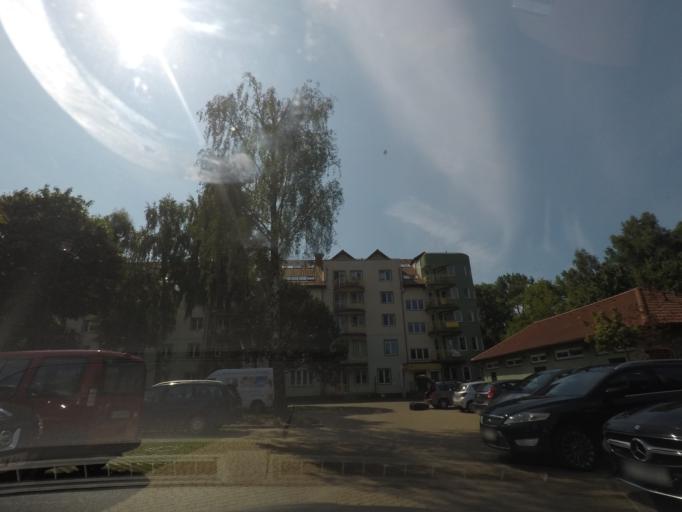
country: PL
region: West Pomeranian Voivodeship
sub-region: Powiat kolobrzeski
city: Dygowo
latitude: 54.1935
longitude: 15.6665
